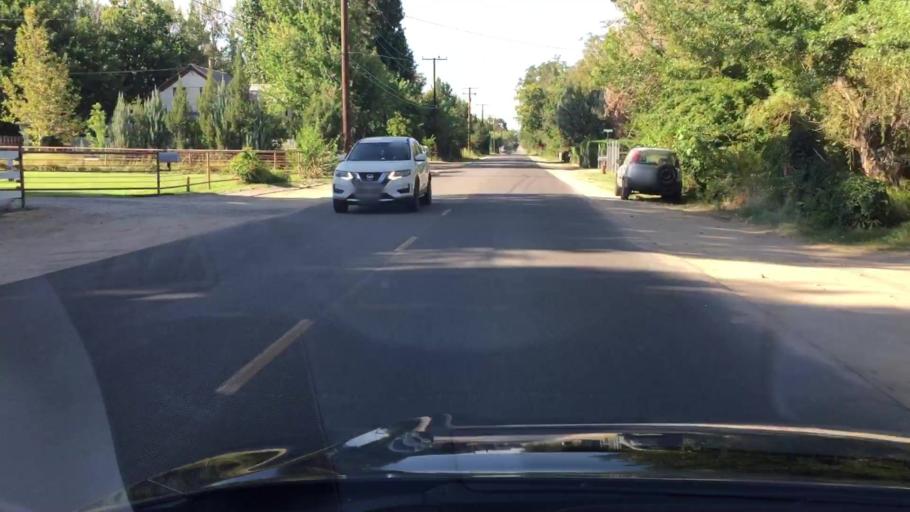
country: US
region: California
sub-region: Inyo County
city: Dixon Lane-Meadow Creek
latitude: 37.3717
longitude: -118.4321
